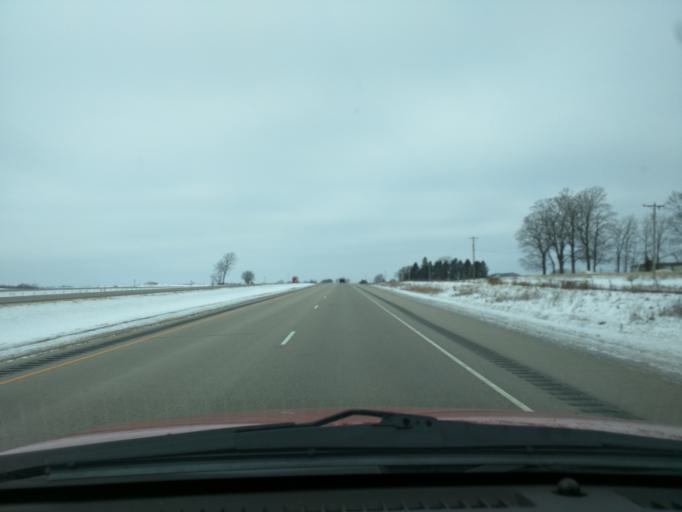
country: US
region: Wisconsin
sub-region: Trempealeau County
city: Trempealeau
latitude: 43.9248
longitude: -91.4678
